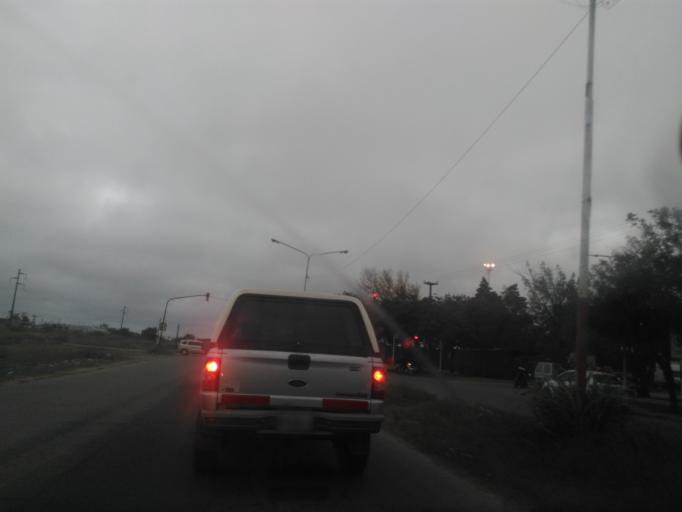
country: AR
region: Chaco
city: Resistencia
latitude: -27.4573
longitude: -59.0228
